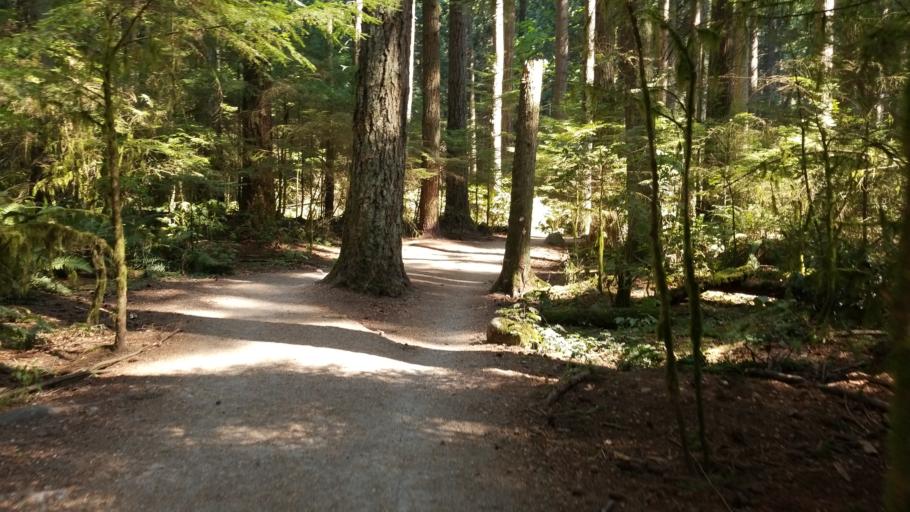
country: CA
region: British Columbia
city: West End
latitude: 49.2520
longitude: -123.2257
